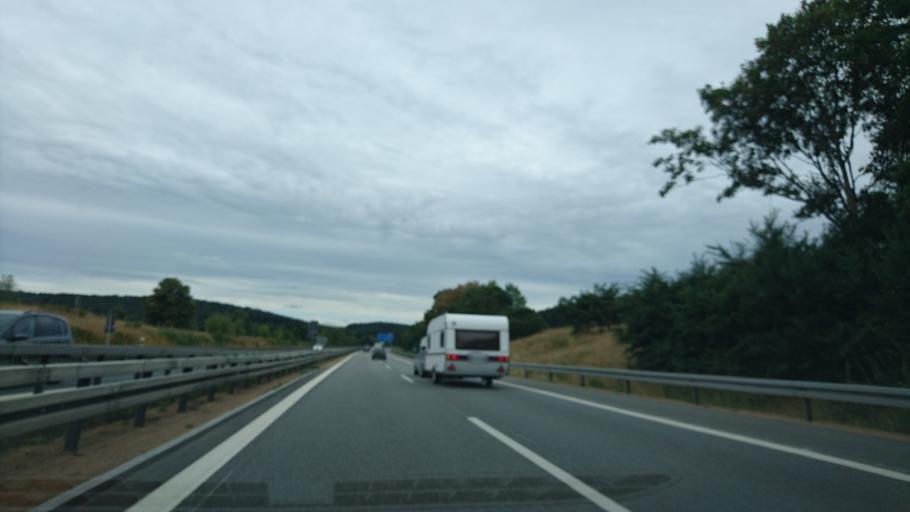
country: DE
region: Bavaria
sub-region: Upper Palatinate
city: Pfreimd
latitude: 49.5084
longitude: 12.1766
